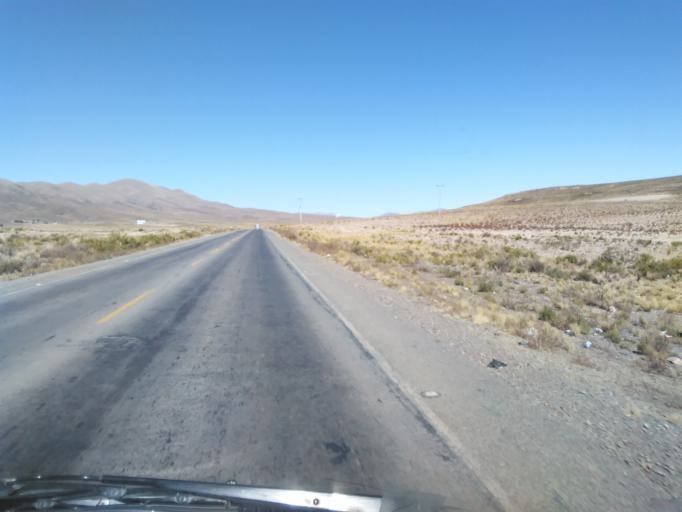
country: BO
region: Oruro
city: Machacamarca
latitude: -18.0467
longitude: -67.0123
